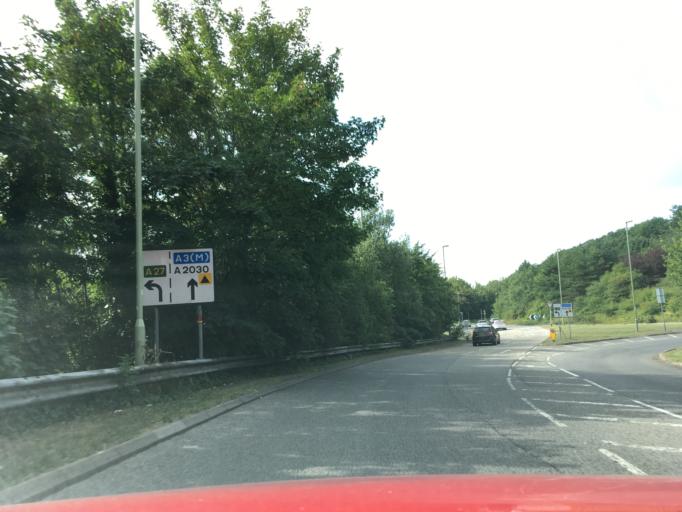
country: GB
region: England
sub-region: Hampshire
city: Havant
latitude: 50.8510
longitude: -1.0101
